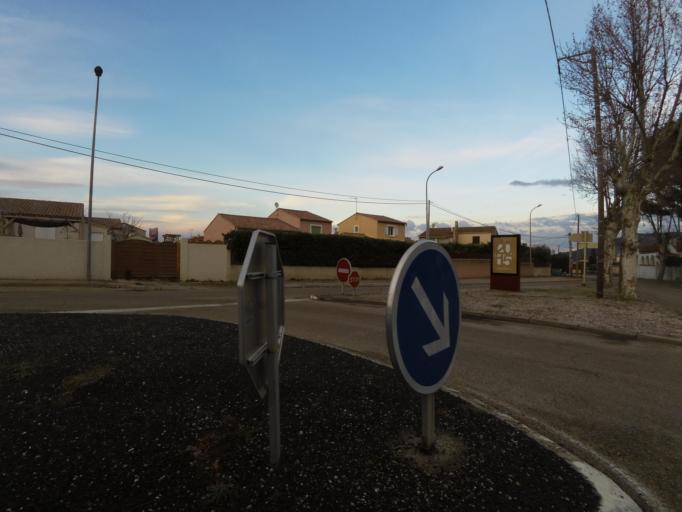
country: FR
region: Languedoc-Roussillon
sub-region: Departement du Gard
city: Calvisson
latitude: 43.7898
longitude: 4.2007
